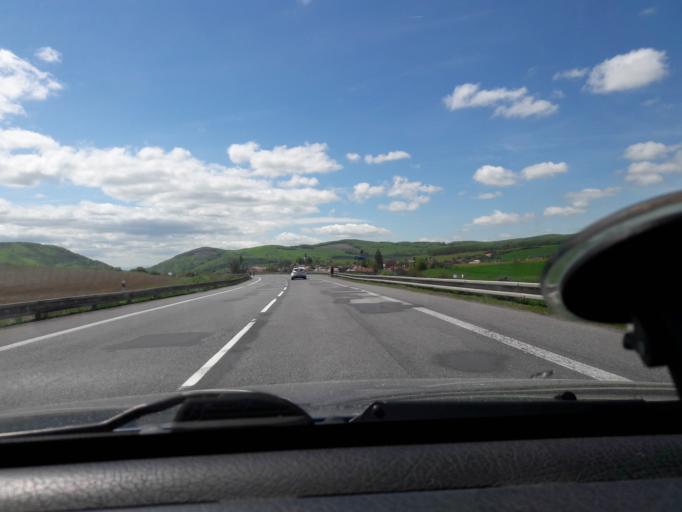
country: SK
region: Banskobystricky
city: Krupina
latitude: 48.4430
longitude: 19.0976
